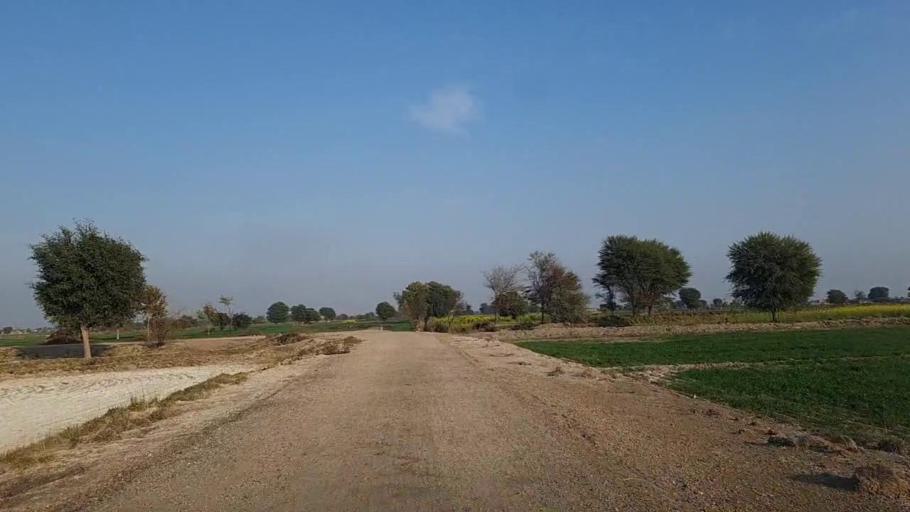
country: PK
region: Sindh
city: Jam Sahib
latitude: 26.3769
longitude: 68.5280
